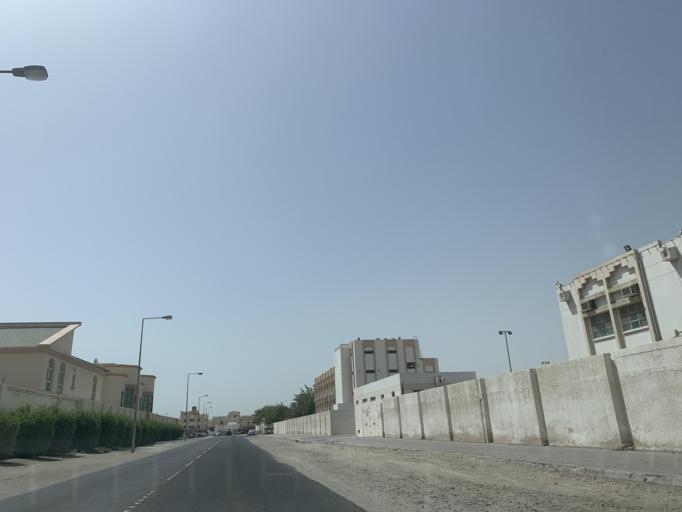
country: BH
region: Northern
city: Ar Rifa'
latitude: 26.1545
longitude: 50.5792
